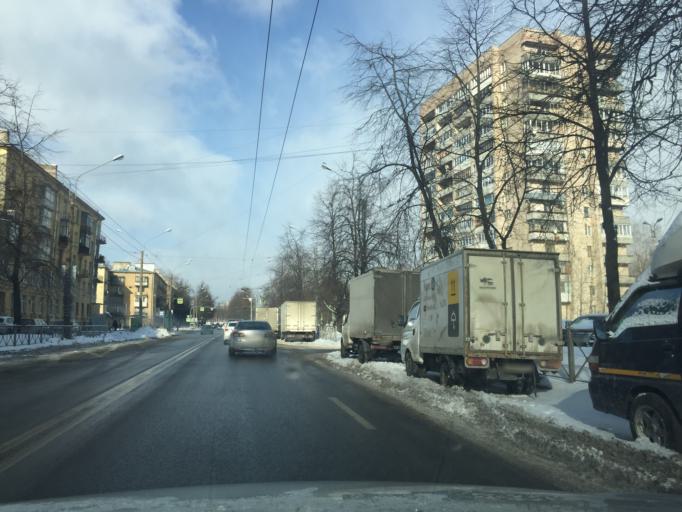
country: RU
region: Leningrad
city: Kalininskiy
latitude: 59.9583
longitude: 30.4223
